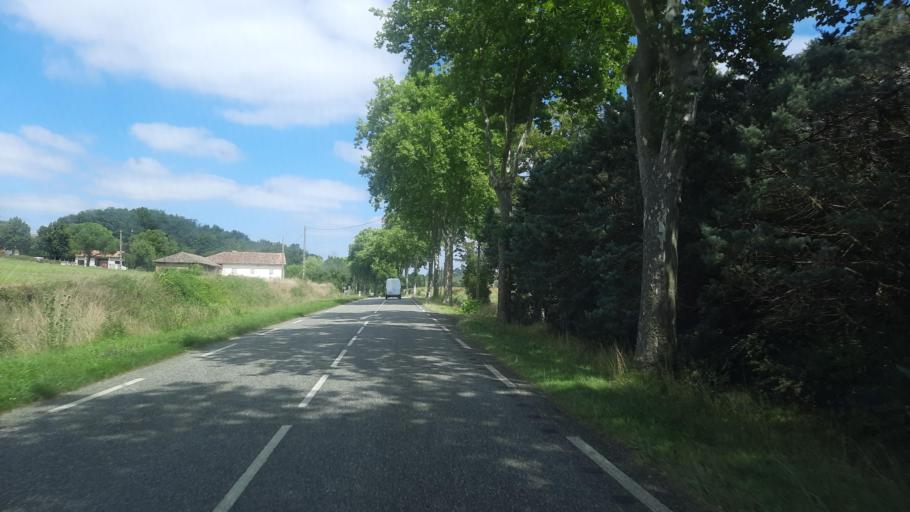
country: FR
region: Midi-Pyrenees
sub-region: Departement de la Haute-Garonne
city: Boulogne-sur-Gesse
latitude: 43.3632
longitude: 0.7385
